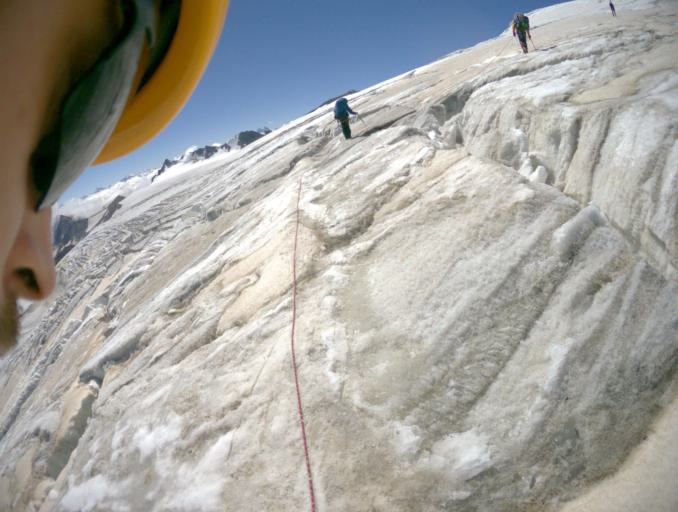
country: RU
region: Kabardino-Balkariya
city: Terskol
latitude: 43.3626
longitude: 42.4988
